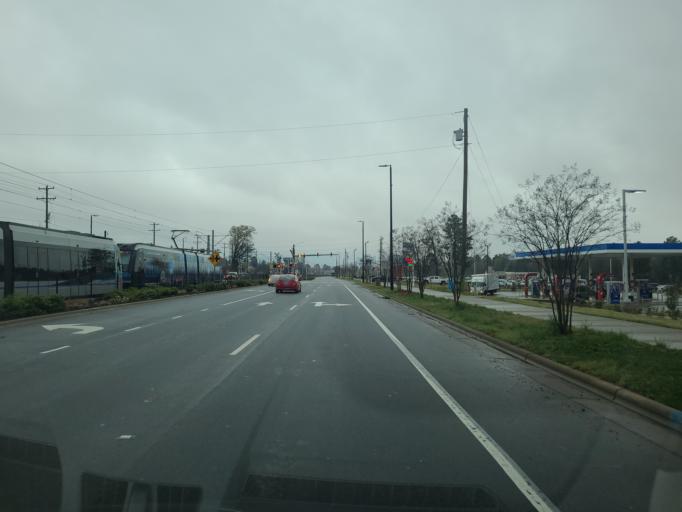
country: US
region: North Carolina
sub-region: Mecklenburg County
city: Charlotte
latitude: 35.2716
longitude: -80.7682
